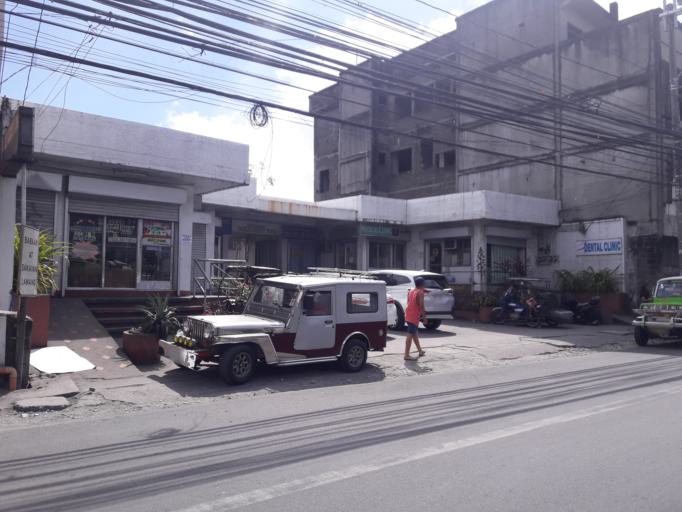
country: PH
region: Calabarzon
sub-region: Province of Laguna
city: Santa Rosa
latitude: 14.3068
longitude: 121.1103
